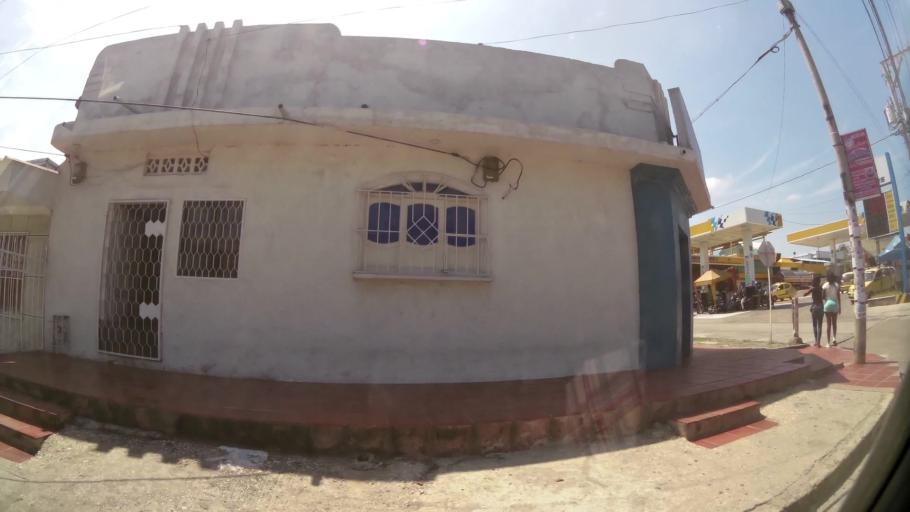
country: CO
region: Atlantico
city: Barranquilla
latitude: 10.9687
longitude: -74.8088
